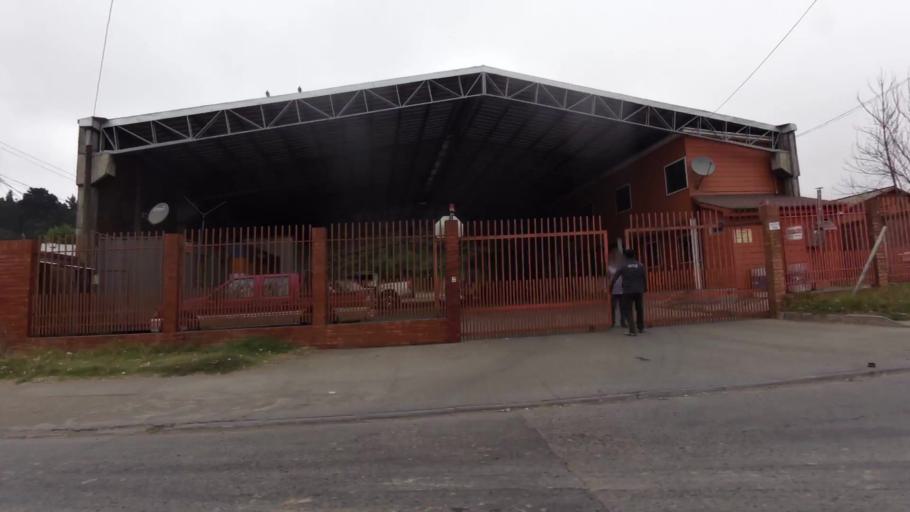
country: CL
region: Biobio
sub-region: Provincia de Concepcion
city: Concepcion
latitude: -36.8219
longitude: -73.0060
